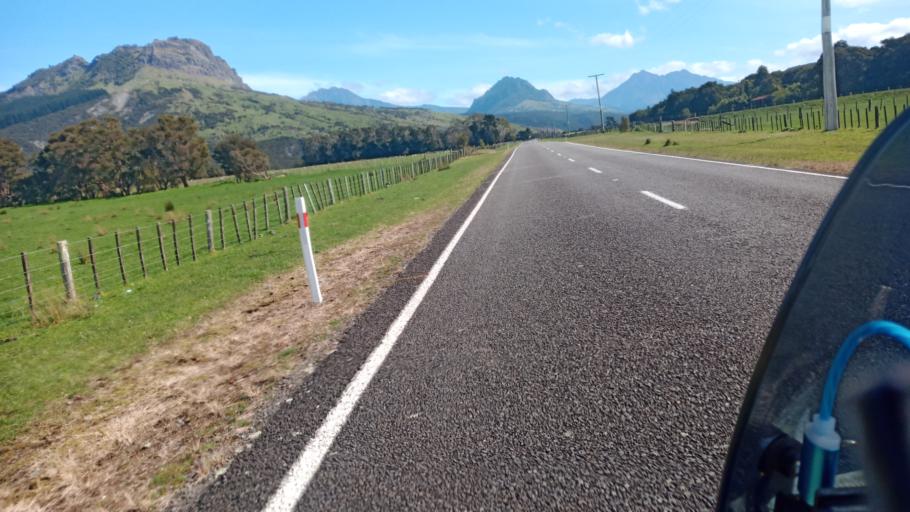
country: NZ
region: Gisborne
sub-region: Gisborne District
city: Gisborne
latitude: -37.8650
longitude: 178.2199
